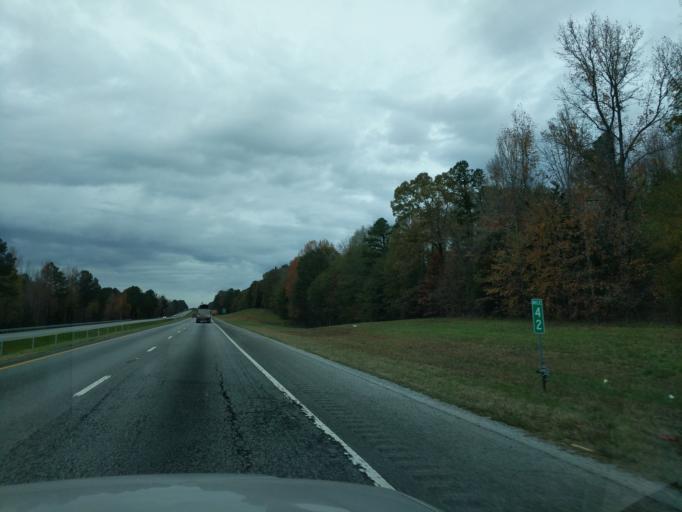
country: US
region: South Carolina
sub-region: Laurens County
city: Watts Mills
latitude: 34.6453
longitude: -81.9155
